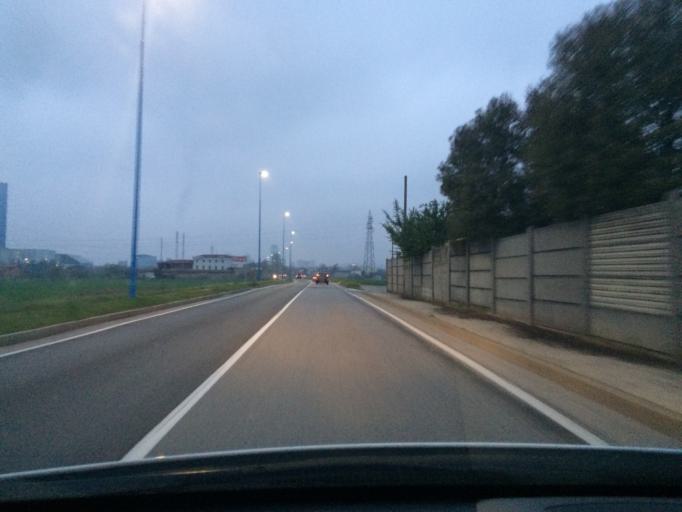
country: IT
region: Lombardy
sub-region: Provincia di Brescia
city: Folzano
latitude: 45.5034
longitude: 10.2145
